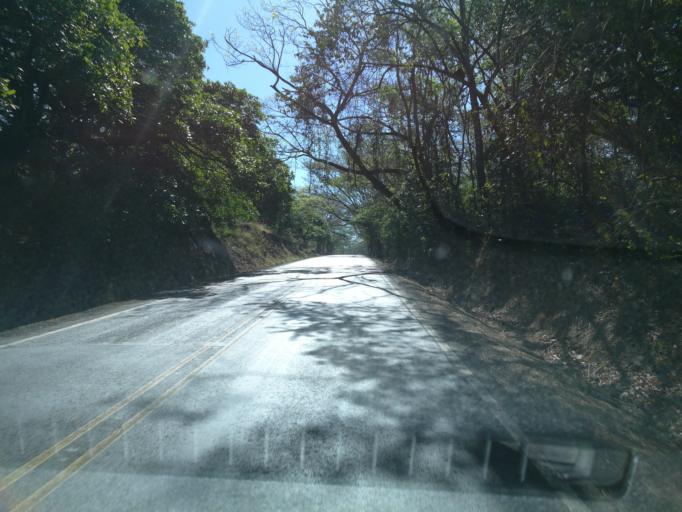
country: CR
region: Puntarenas
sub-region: Canton Central de Puntarenas
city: Puntarenas
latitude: 10.1016
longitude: -84.8718
